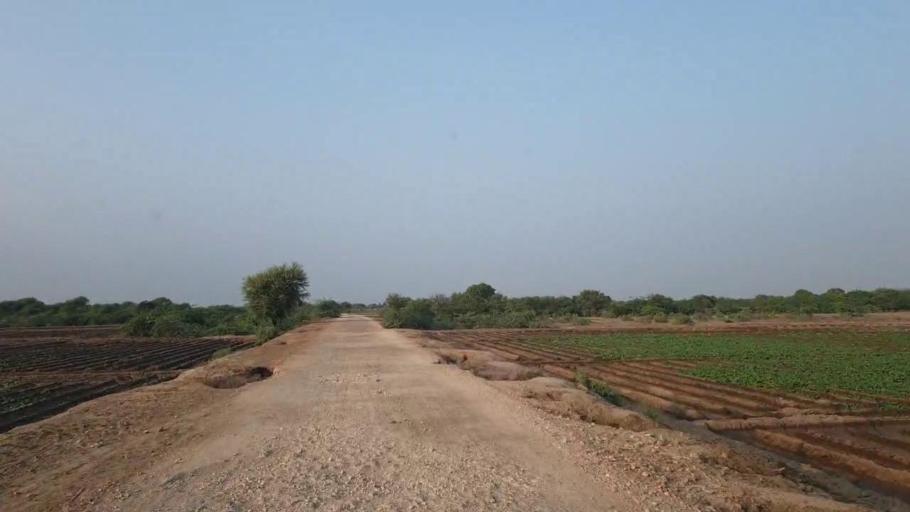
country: PK
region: Sindh
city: Rajo Khanani
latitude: 25.0316
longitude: 68.9773
